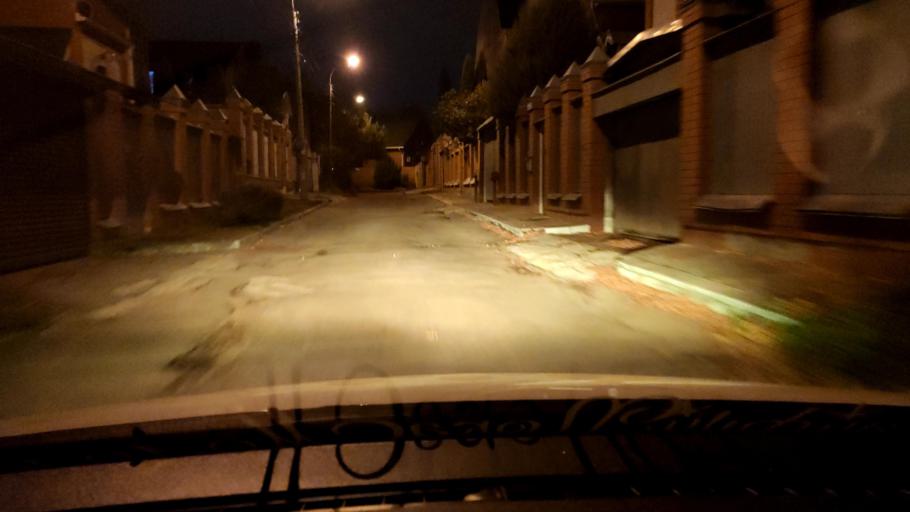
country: RU
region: Voronezj
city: Voronezh
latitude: 51.7081
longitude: 39.1979
